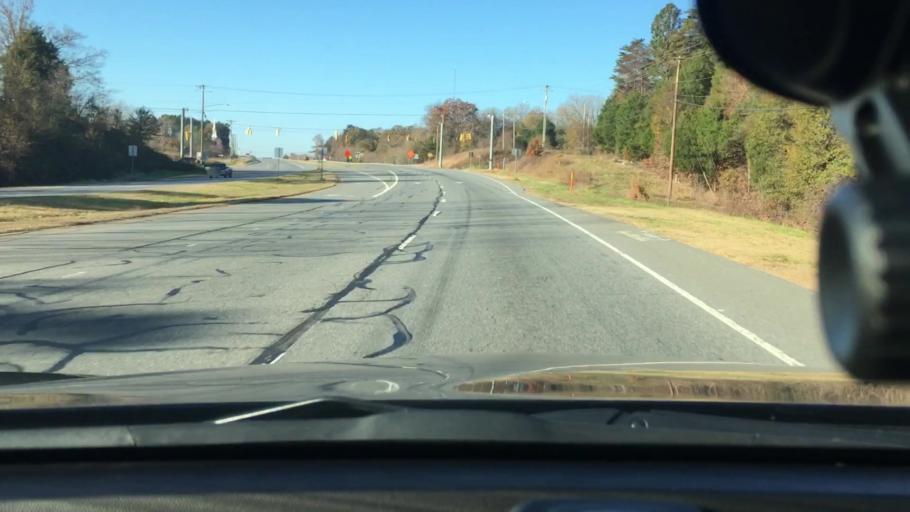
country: US
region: North Carolina
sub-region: Cabarrus County
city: Concord
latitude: 35.3681
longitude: -80.5765
